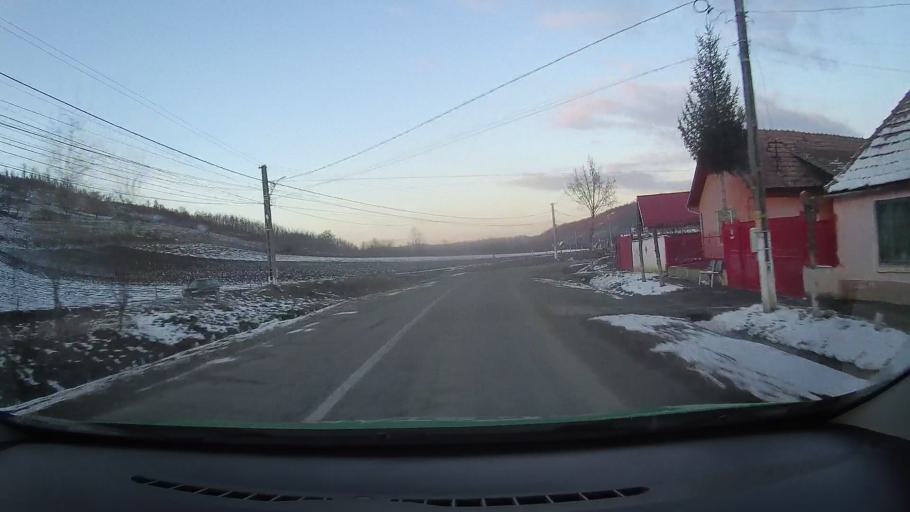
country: RO
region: Sibiu
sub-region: Comuna Alma
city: Alma
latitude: 46.1933
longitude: 24.4709
